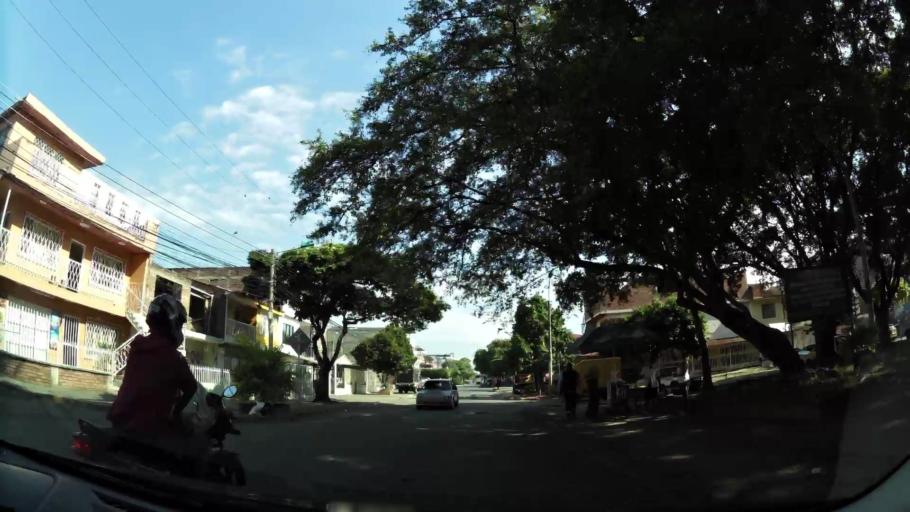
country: CO
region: Valle del Cauca
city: Cali
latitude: 3.4231
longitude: -76.5157
